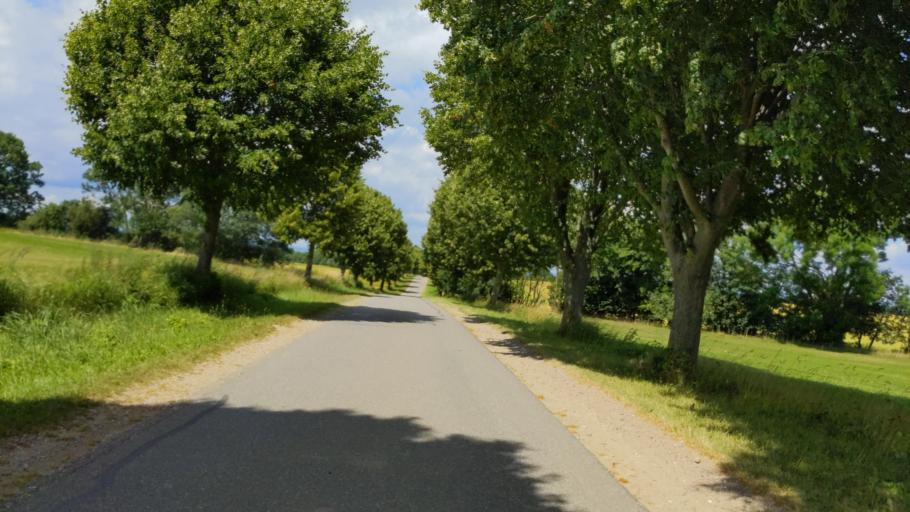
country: DE
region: Mecklenburg-Vorpommern
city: Kalkhorst
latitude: 53.9886
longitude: 11.0798
